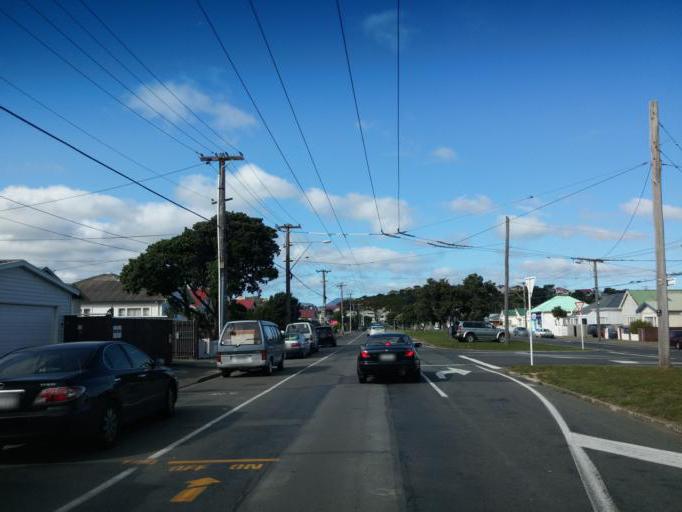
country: NZ
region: Wellington
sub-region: Wellington City
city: Wellington
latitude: -41.3184
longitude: 174.7983
